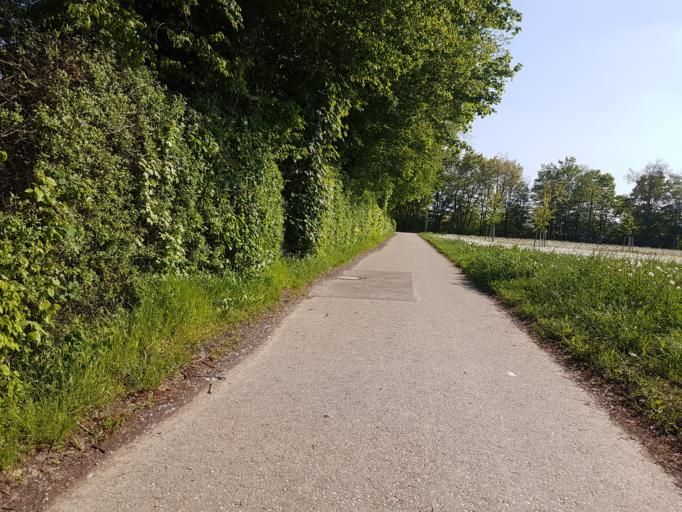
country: DE
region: Baden-Wuerttemberg
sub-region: Regierungsbezirk Stuttgart
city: Ludwigsburg
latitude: 48.8854
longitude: 9.1756
